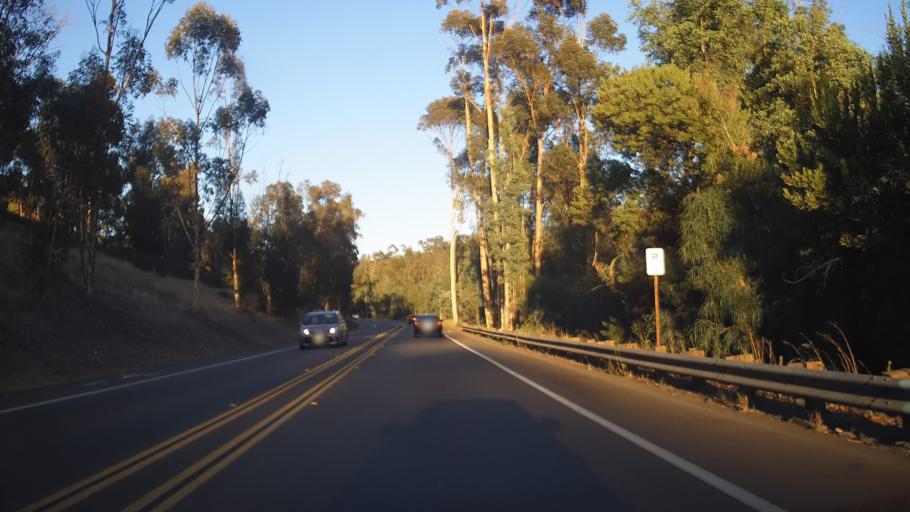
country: US
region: California
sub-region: San Diego County
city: Poway
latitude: 32.9059
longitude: -117.0813
